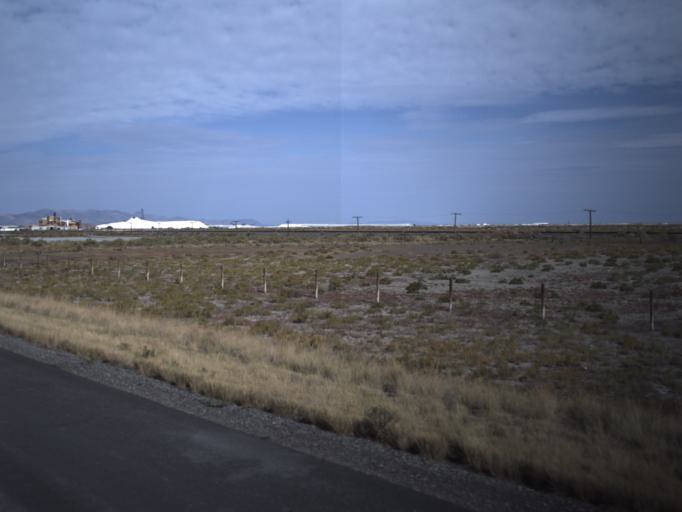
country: US
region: Utah
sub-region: Tooele County
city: Grantsville
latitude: 40.7022
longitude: -112.4944
